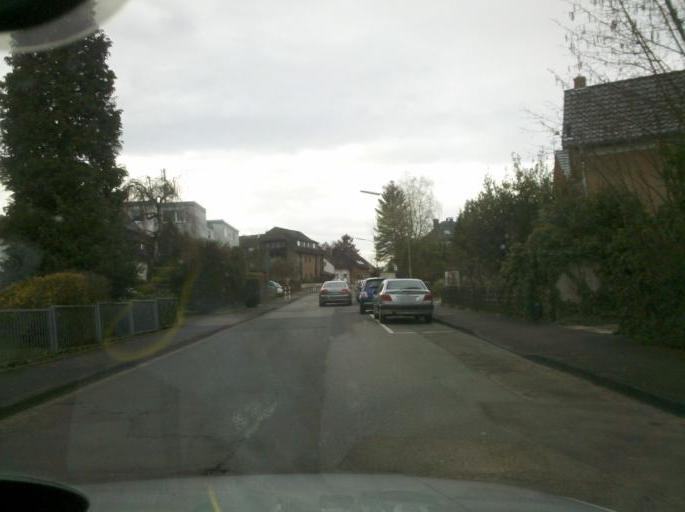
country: DE
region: North Rhine-Westphalia
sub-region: Regierungsbezirk Koln
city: Rosrath
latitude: 50.9000
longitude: 7.1771
